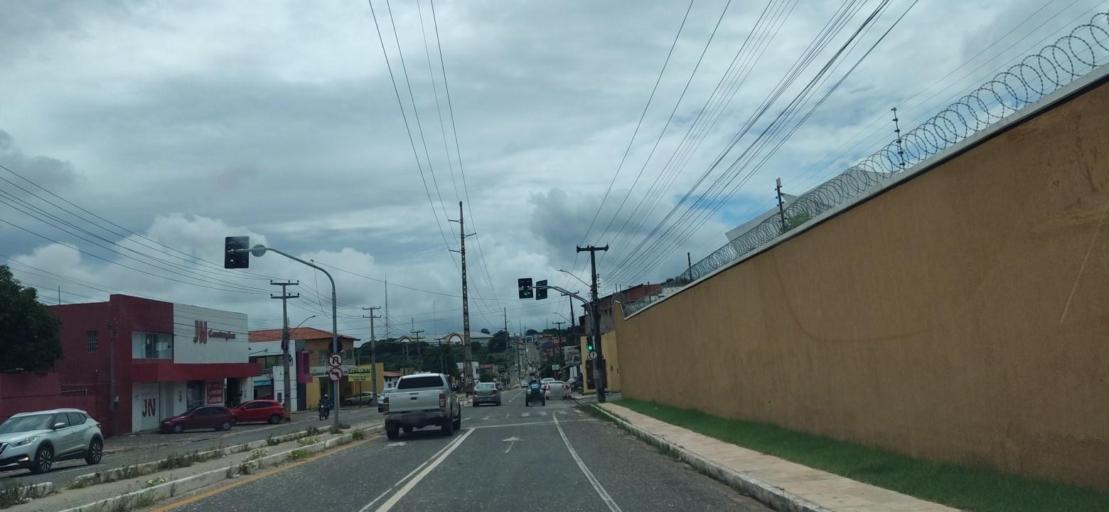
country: BR
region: Piaui
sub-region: Teresina
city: Teresina
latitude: -5.0602
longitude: -42.7549
